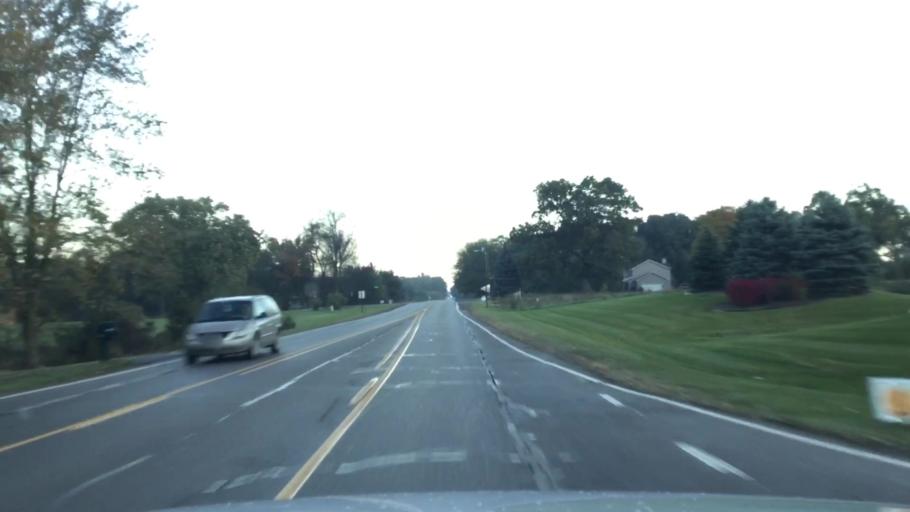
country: US
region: Michigan
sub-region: Livingston County
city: Howell
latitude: 42.6499
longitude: -83.9352
